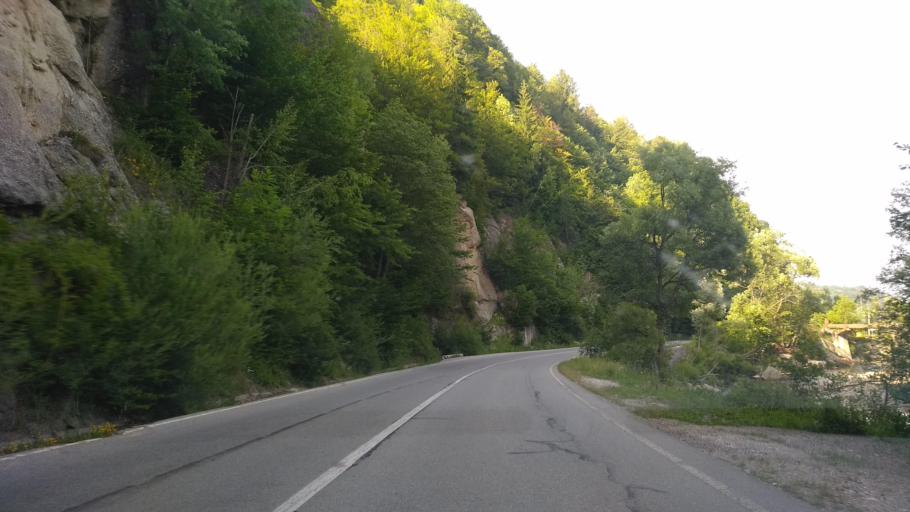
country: RO
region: Hunedoara
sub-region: Comuna Uricani
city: Uricani
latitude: 45.3180
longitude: 23.0795
